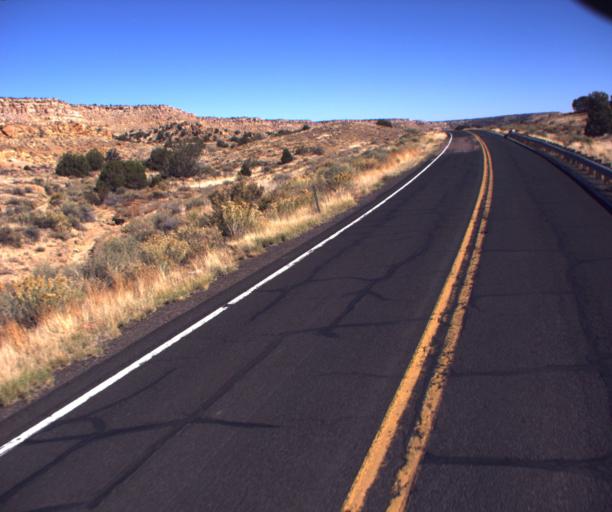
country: US
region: Arizona
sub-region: Navajo County
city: First Mesa
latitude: 35.8307
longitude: -110.2740
